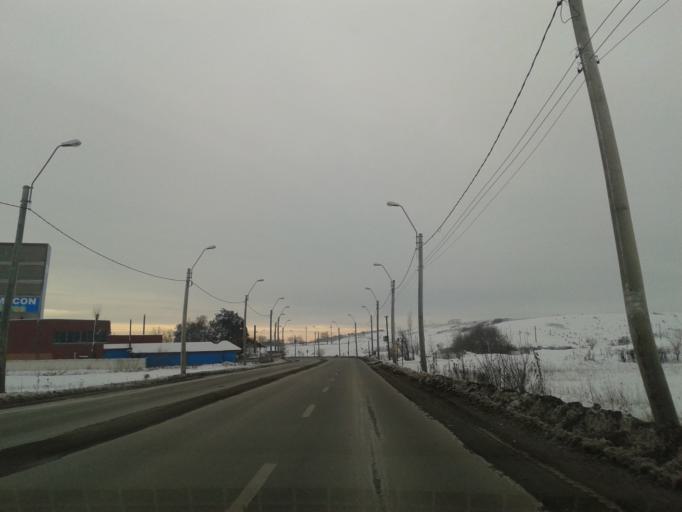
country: RO
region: Hunedoara
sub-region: Municipiul Deva
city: Cristur
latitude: 45.8454
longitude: 22.9499
